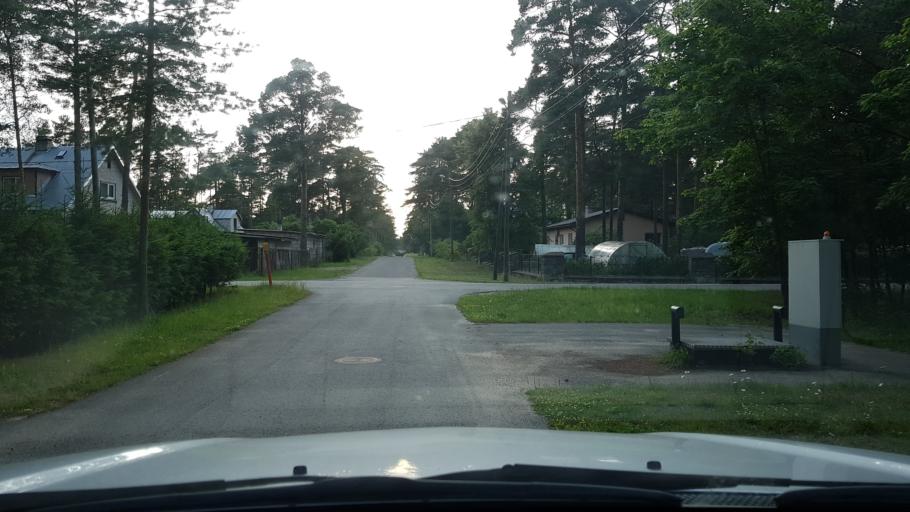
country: EE
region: Ida-Virumaa
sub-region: Narva-Joesuu linn
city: Narva-Joesuu
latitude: 59.4539
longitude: 28.0581
